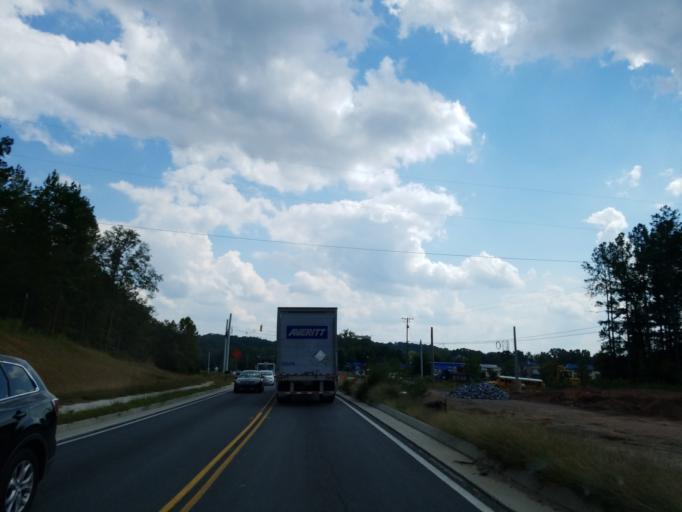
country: US
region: Georgia
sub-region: Gwinnett County
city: Sugar Hill
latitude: 34.1307
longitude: -84.0980
